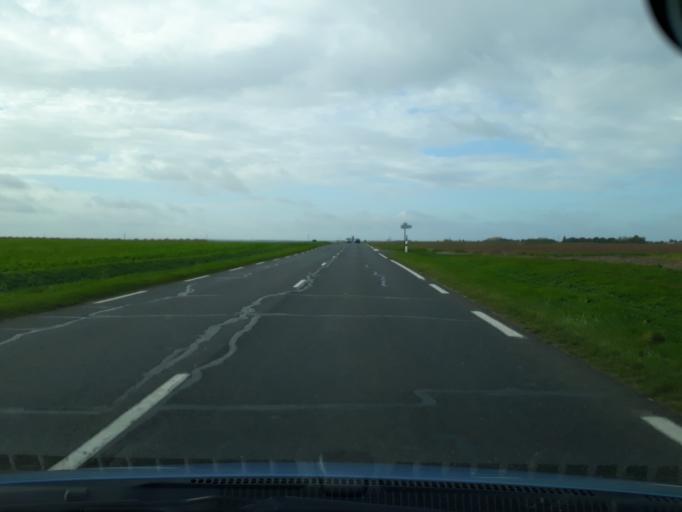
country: FR
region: Centre
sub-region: Departement du Loiret
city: Pithiviers-le-Vieil
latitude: 48.1493
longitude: 2.2217
